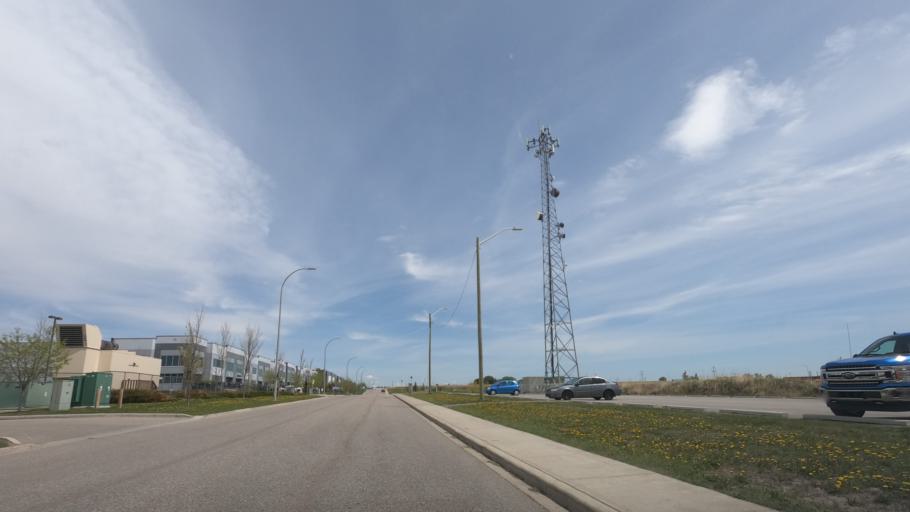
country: CA
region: Alberta
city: Airdrie
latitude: 51.3027
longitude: -113.9893
